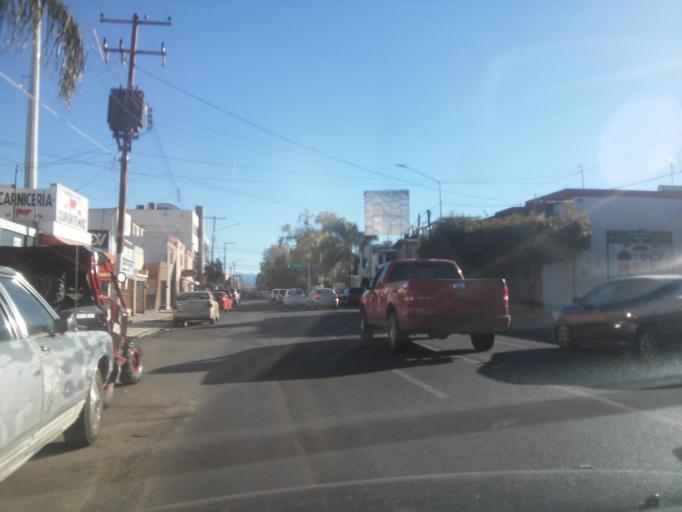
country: MX
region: Durango
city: Victoria de Durango
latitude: 24.0327
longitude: -104.6570
